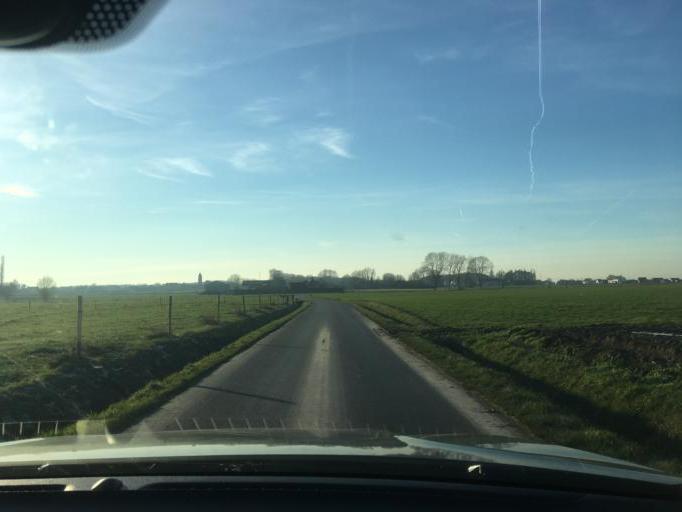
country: BE
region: Flanders
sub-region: Provincie West-Vlaanderen
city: Pittem
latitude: 50.9652
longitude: 3.2551
